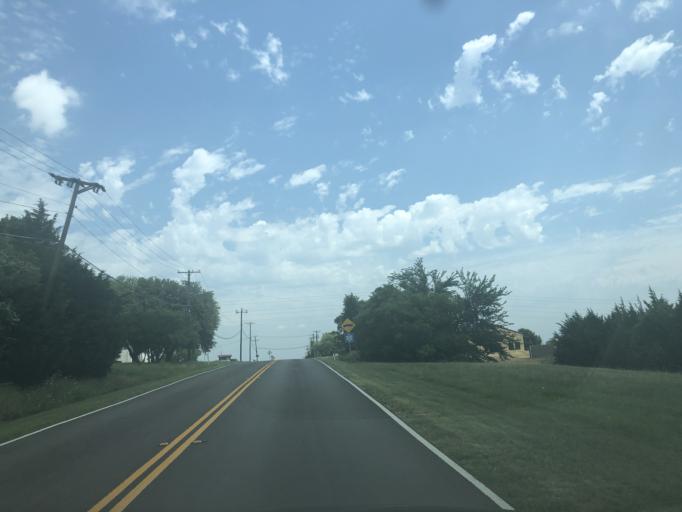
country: US
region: Texas
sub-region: Dallas County
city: Grand Prairie
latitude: 32.7218
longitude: -97.0196
